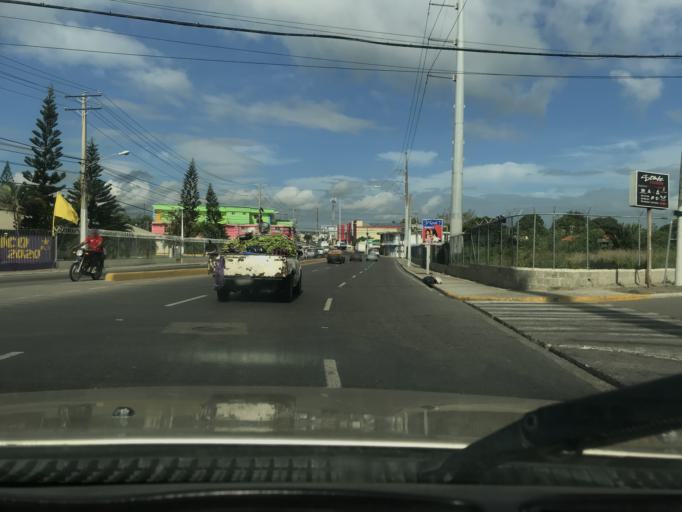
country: DO
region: Santiago
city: Santiago de los Caballeros
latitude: 19.4857
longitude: -70.7330
